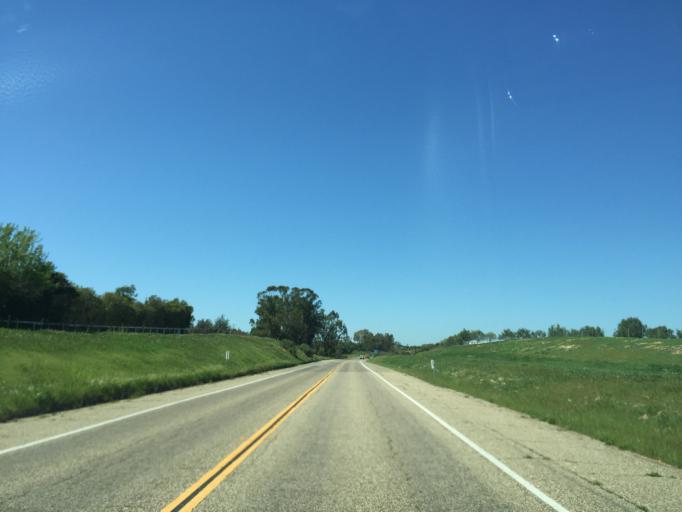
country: US
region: California
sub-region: Santa Barbara County
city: Santa Ynez
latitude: 34.6269
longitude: -120.0746
